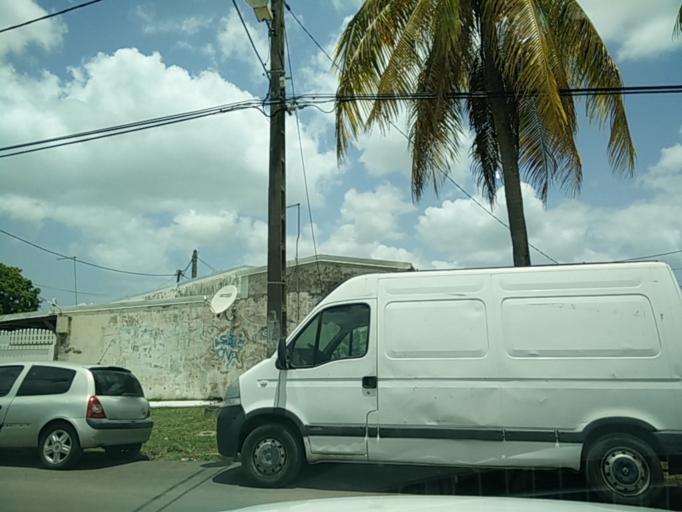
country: GP
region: Guadeloupe
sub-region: Guadeloupe
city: Pointe-a-Pitre
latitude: 16.2589
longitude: -61.5293
